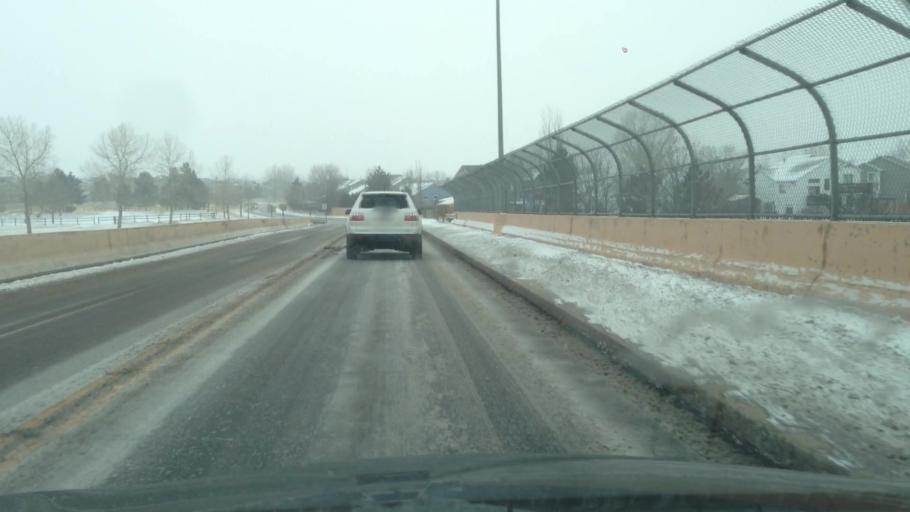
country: US
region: Colorado
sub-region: Douglas County
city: Stonegate
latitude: 39.5563
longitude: -104.7864
